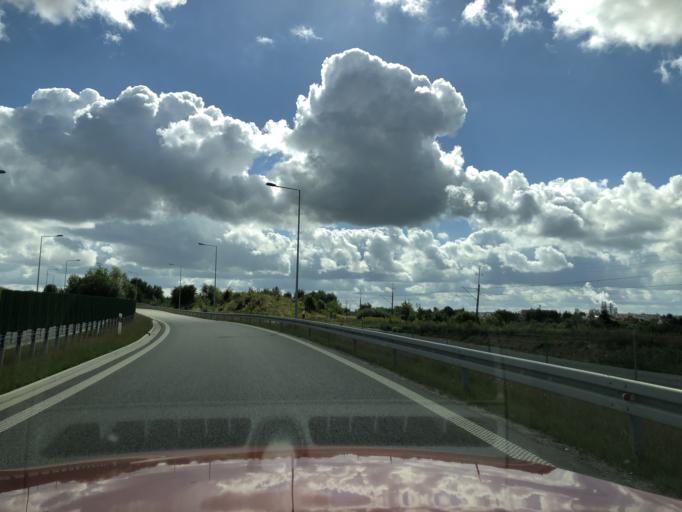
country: PL
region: West Pomeranian Voivodeship
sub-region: Powiat szczecinecki
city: Szczecinek
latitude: 53.7111
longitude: 16.7173
